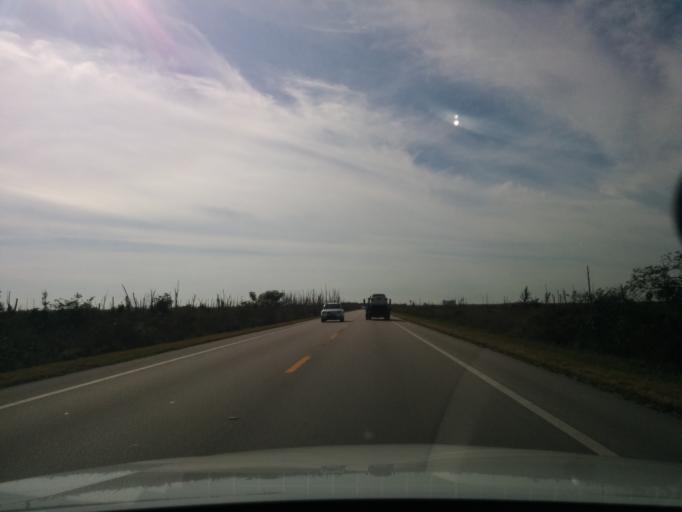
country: US
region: Florida
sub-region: Miami-Dade County
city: Tamiami
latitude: 25.7944
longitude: -80.4825
